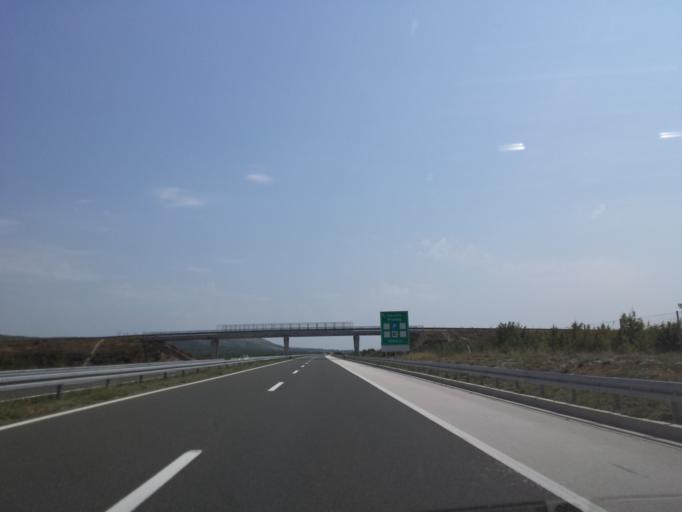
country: HR
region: Zadarska
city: Benkovac
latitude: 43.9563
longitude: 15.6736
